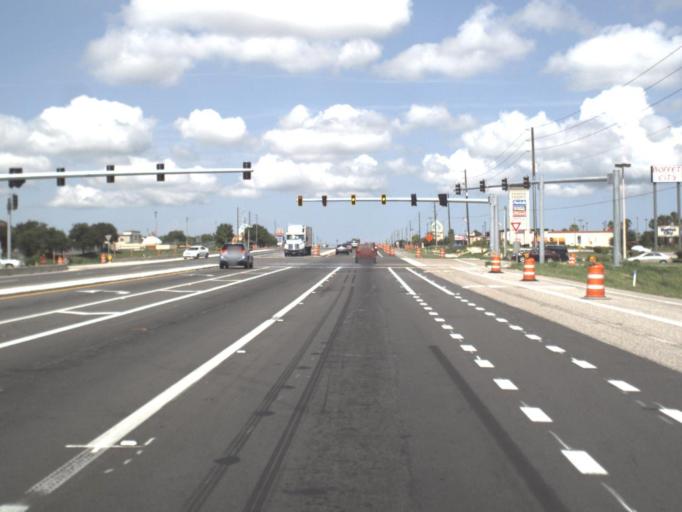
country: US
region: Florida
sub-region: Hernando County
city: Brookridge
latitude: 28.5338
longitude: -82.5043
